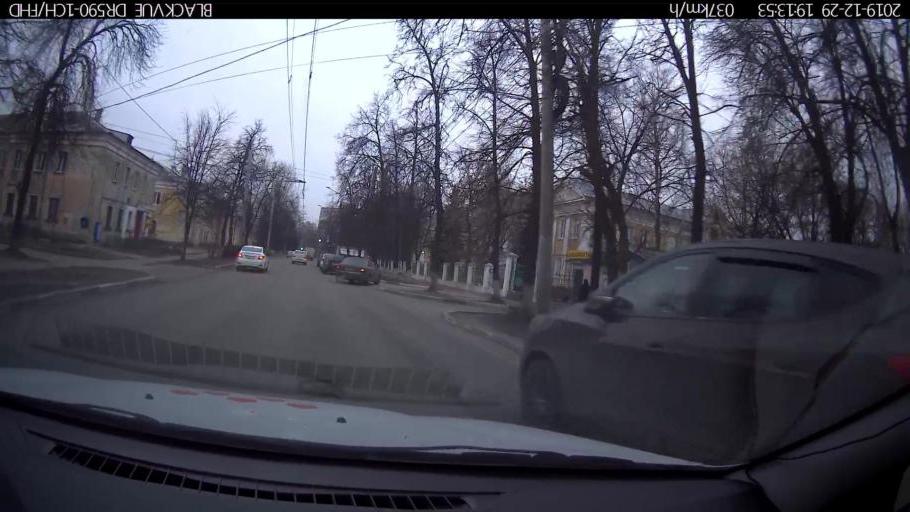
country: RU
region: Nizjnij Novgorod
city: Nizhniy Novgorod
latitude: 56.3277
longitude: 43.8782
